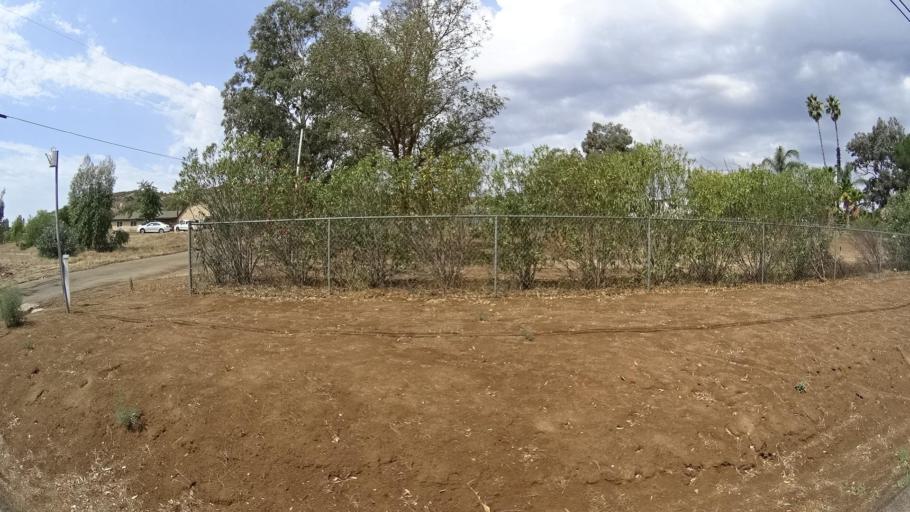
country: US
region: California
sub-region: San Diego County
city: Ramona
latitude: 33.0808
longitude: -116.8394
